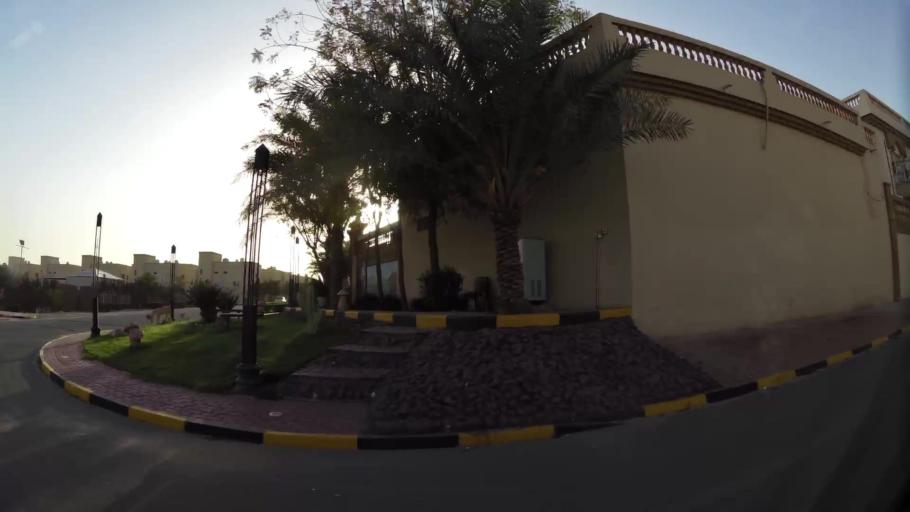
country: QA
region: Baladiyat ar Rayyan
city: Ar Rayyan
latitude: 25.3233
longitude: 51.4581
